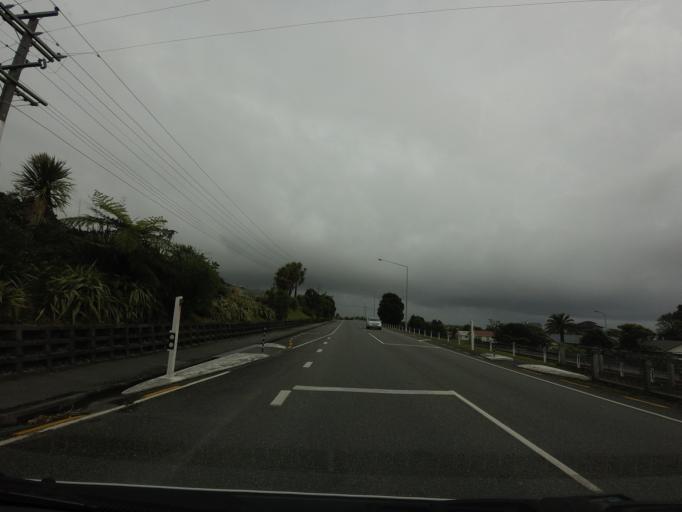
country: NZ
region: West Coast
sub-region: Grey District
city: Greymouth
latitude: -42.4748
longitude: 171.1867
